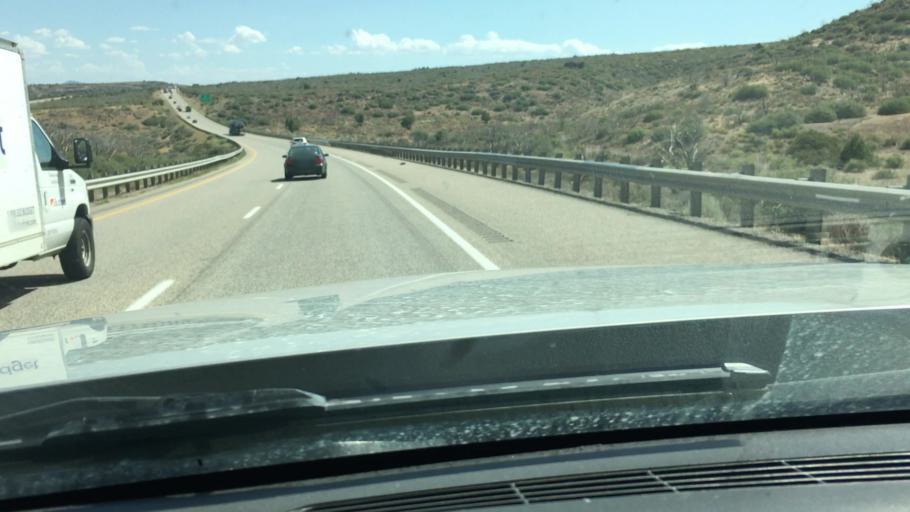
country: US
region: Utah
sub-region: Washington County
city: Toquerville
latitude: 37.3060
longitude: -113.2989
